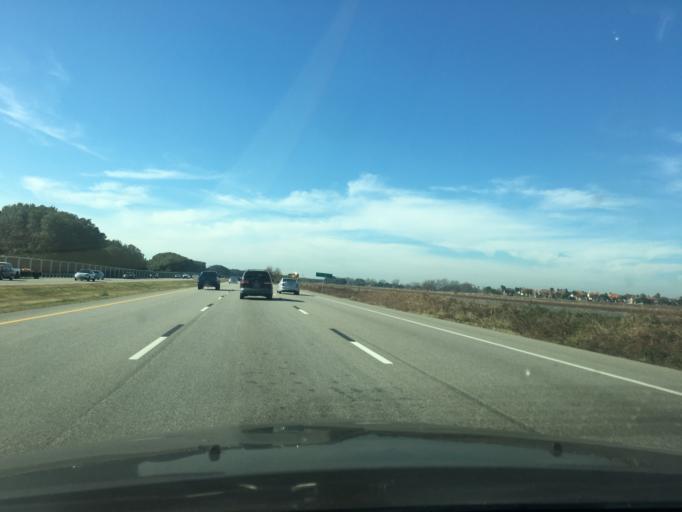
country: US
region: Texas
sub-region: Fort Bend County
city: New Territory
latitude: 29.6058
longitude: -95.6674
